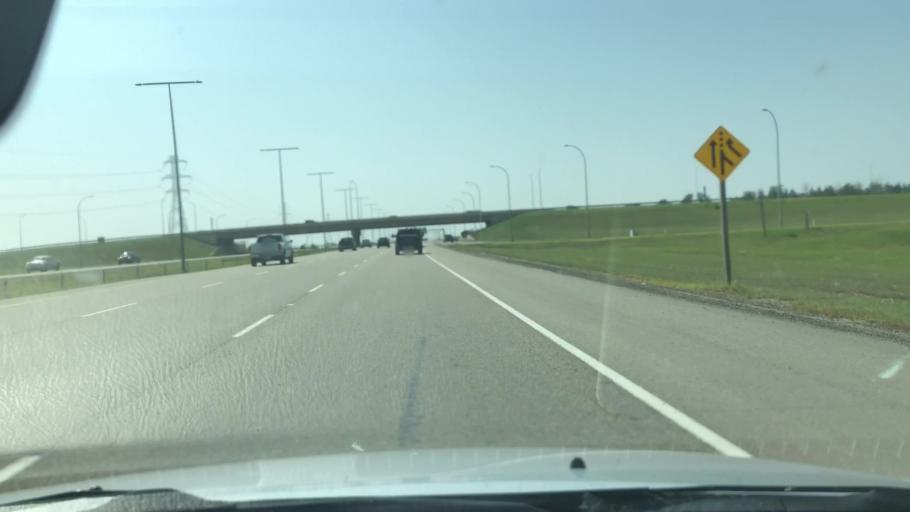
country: CA
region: Alberta
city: St. Albert
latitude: 53.5255
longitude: -113.6597
